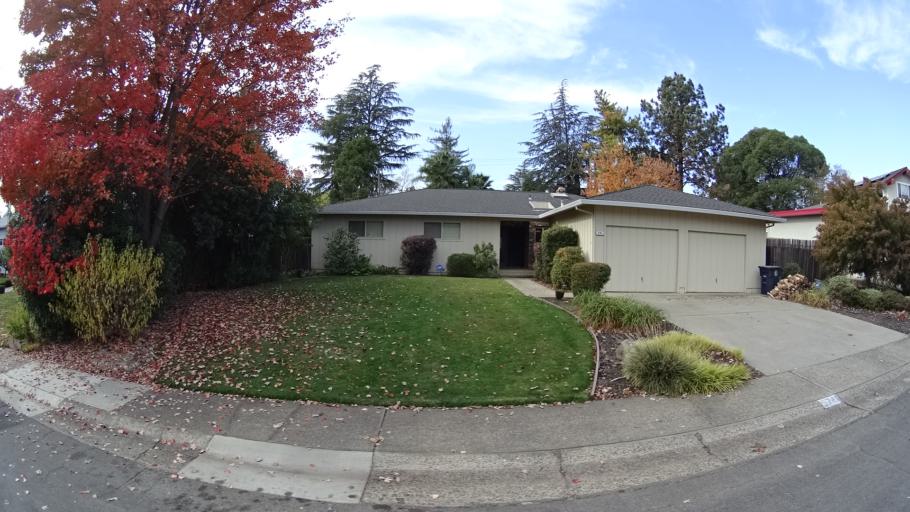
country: US
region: California
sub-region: Sacramento County
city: Fair Oaks
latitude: 38.6702
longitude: -121.2802
